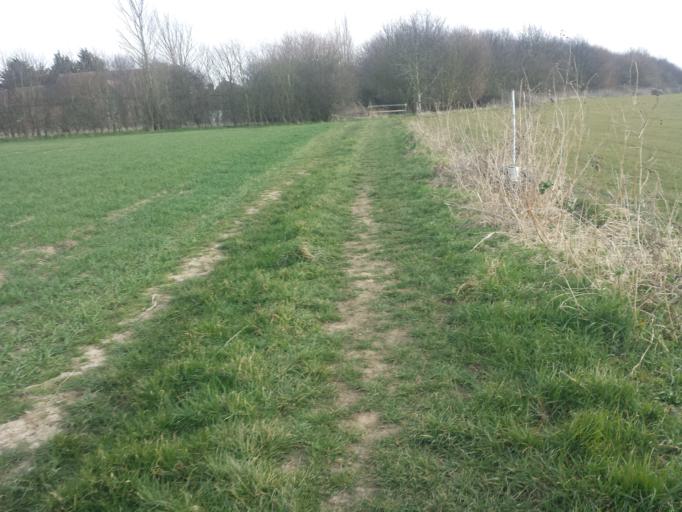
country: GB
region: England
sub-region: Essex
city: Little Clacton
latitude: 51.8780
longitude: 1.1624
